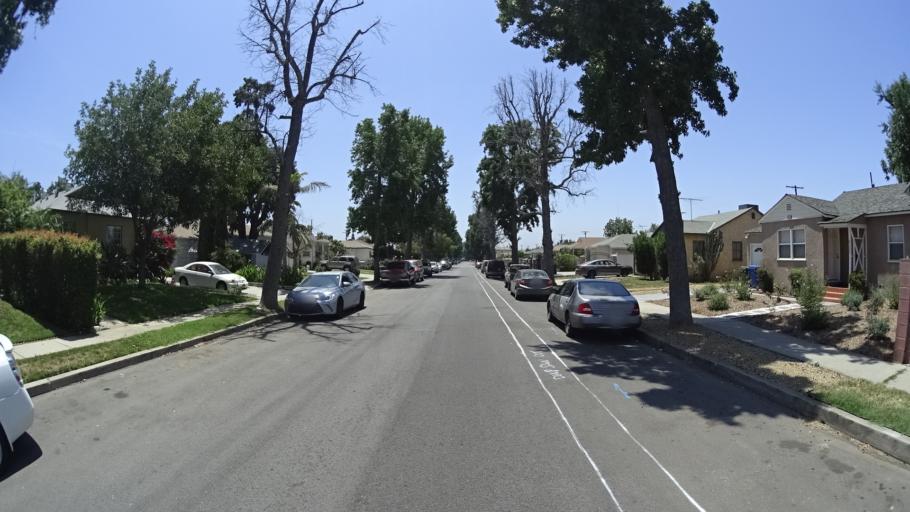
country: US
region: California
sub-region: Los Angeles County
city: Van Nuys
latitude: 34.2191
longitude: -118.4627
